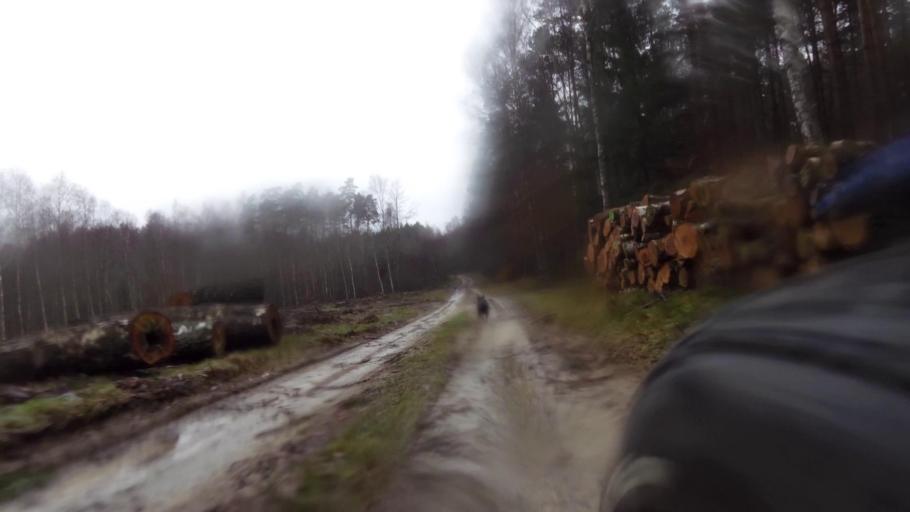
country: PL
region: West Pomeranian Voivodeship
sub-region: Powiat drawski
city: Zlocieniec
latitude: 53.5528
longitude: 15.9371
